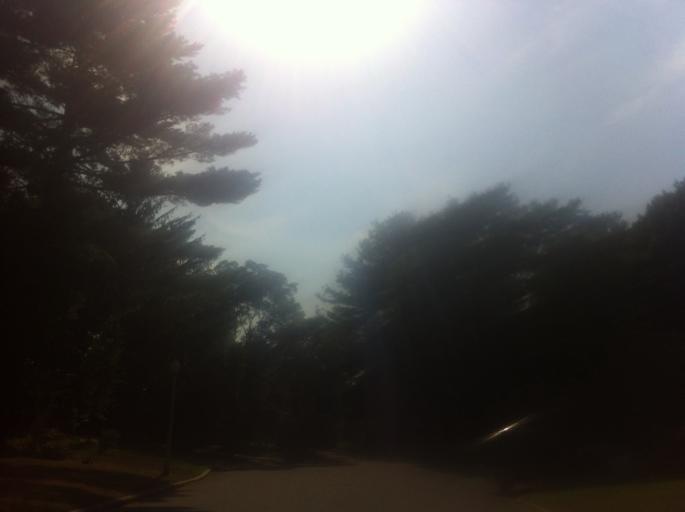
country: US
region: New York
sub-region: Nassau County
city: Locust Valley
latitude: 40.8581
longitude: -73.6027
